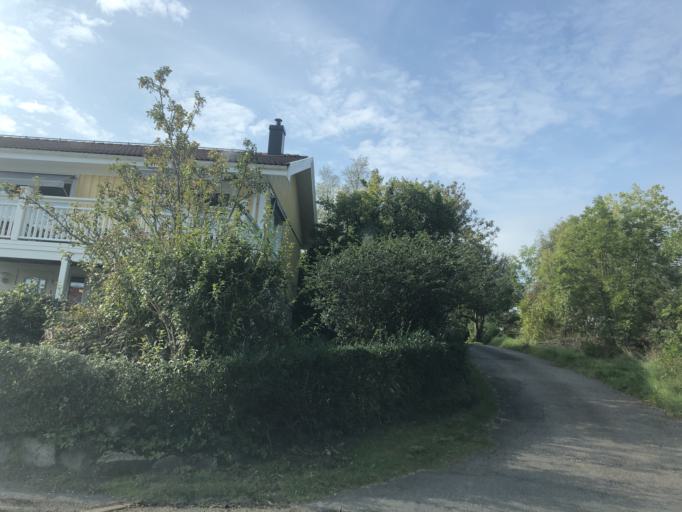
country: SE
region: Vaestra Goetaland
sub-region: Goteborg
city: Majorna
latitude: 57.6446
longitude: 11.8772
